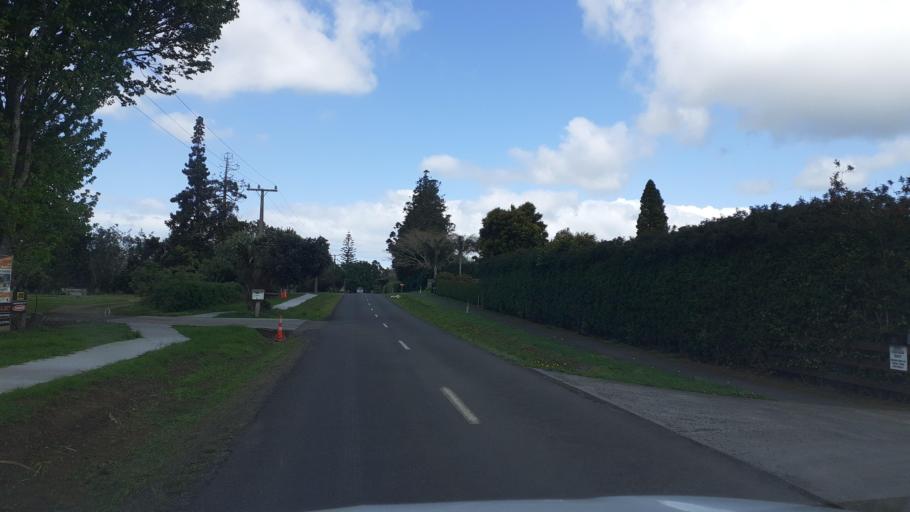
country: NZ
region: Northland
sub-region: Far North District
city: Kerikeri
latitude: -35.2412
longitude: 173.9580
